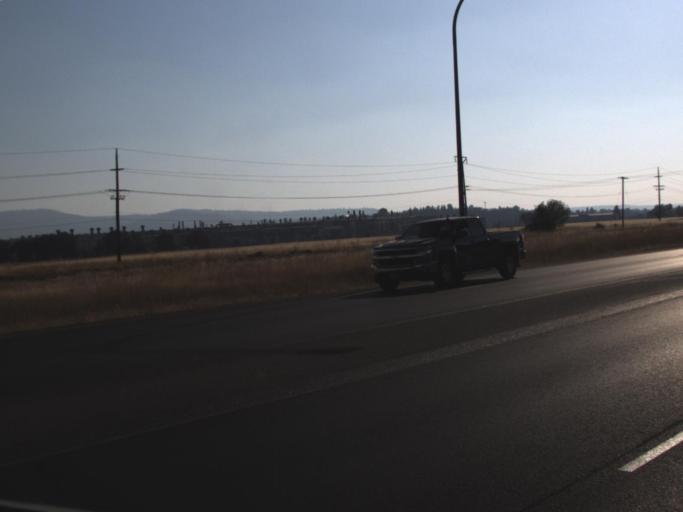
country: US
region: Washington
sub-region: Spokane County
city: Trentwood
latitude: 47.6952
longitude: -117.2053
